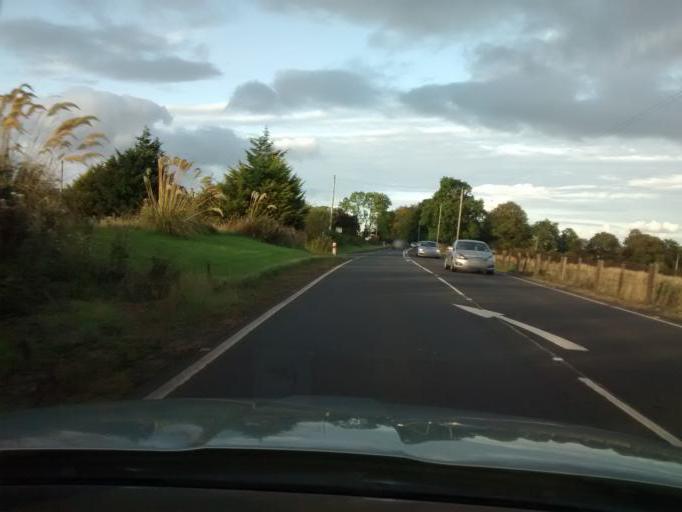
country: GB
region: Scotland
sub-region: Renfrewshire
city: Lochwinnoch
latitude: 55.7960
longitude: -4.5967
